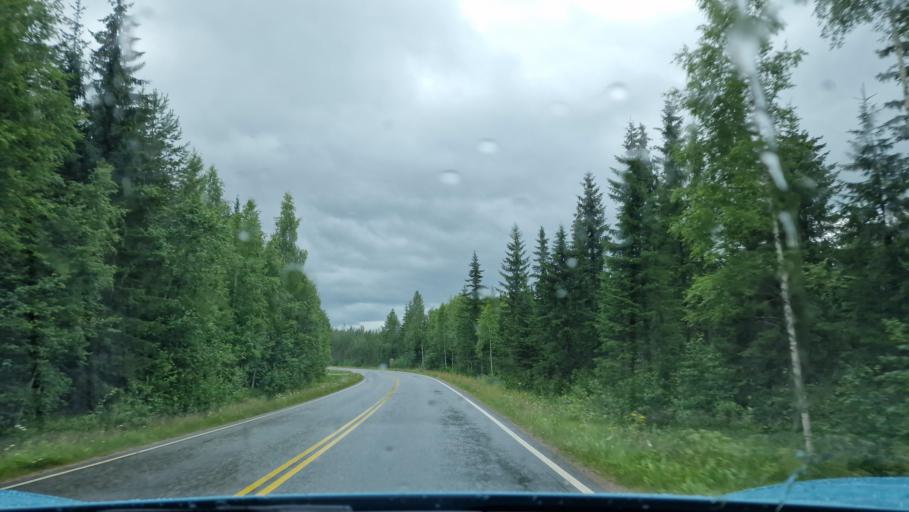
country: FI
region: Southern Ostrobothnia
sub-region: Jaerviseutu
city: Soini
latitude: 62.7833
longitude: 24.3872
